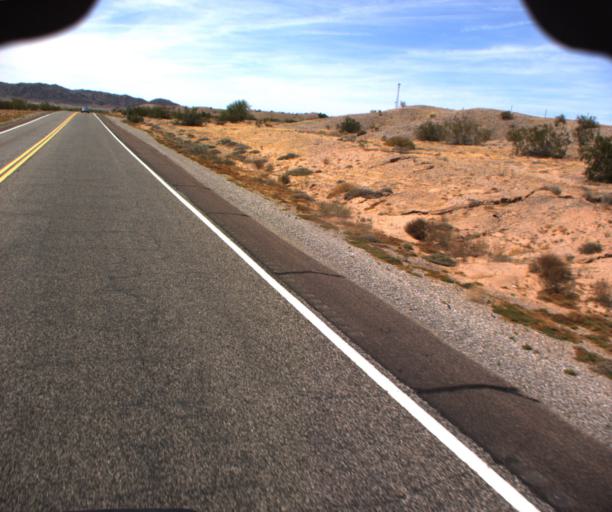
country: US
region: Arizona
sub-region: La Paz County
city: Parker
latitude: 33.9960
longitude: -114.2209
